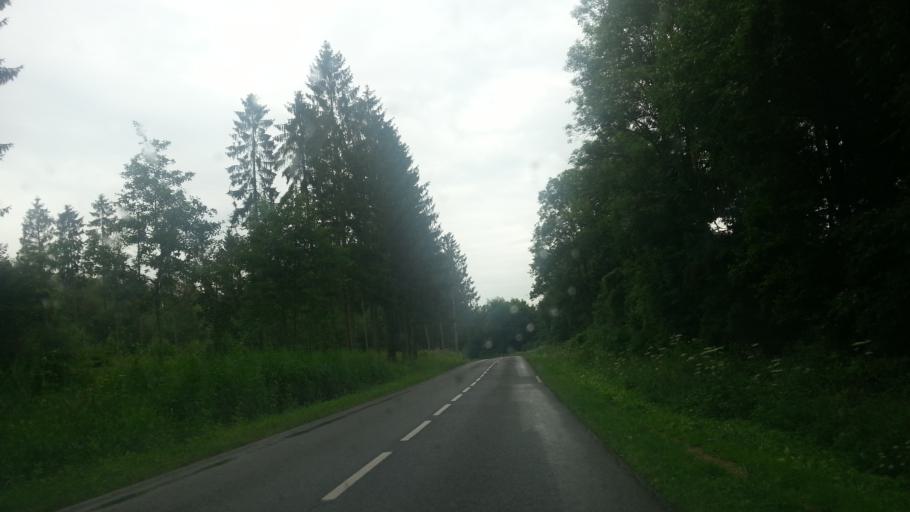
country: FR
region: Lorraine
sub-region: Departement de la Meuse
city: Verdun
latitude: 49.2026
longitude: 5.4227
